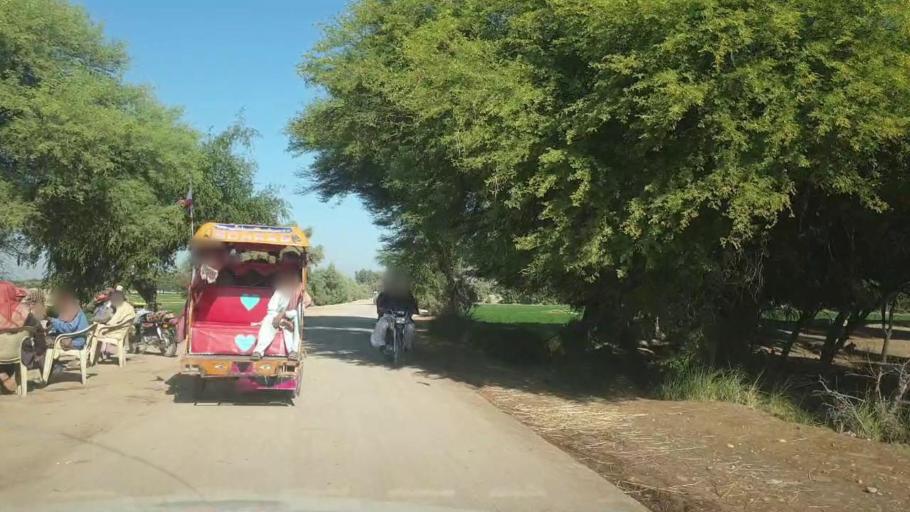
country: PK
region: Sindh
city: Bhan
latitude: 26.5483
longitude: 67.6338
